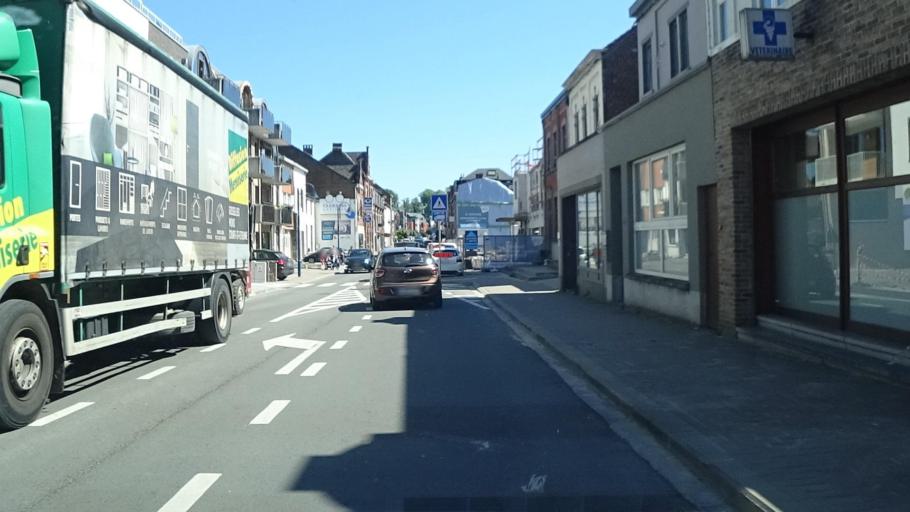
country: BE
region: Wallonia
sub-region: Province du Brabant Wallon
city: Court-Saint-Etienne
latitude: 50.6480
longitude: 4.5638
